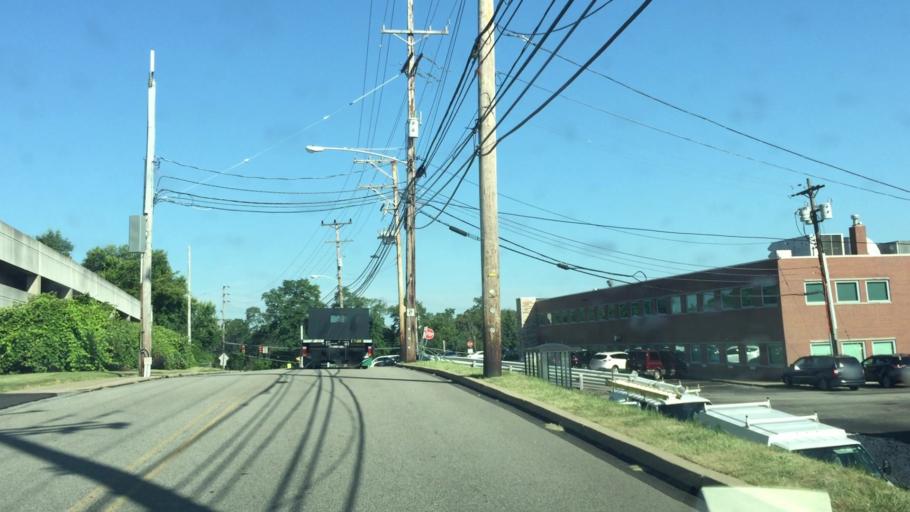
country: US
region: Pennsylvania
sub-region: Allegheny County
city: Green Tree
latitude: 40.4253
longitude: -80.0400
